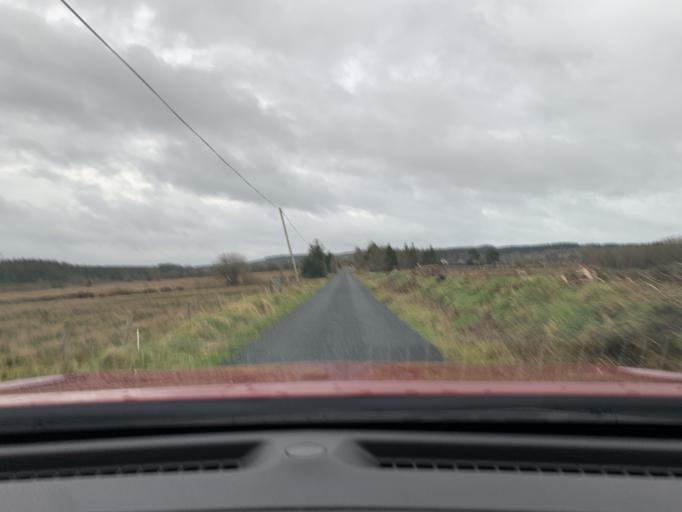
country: IE
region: Connaught
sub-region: Roscommon
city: Ballaghaderreen
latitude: 53.9696
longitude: -8.5230
